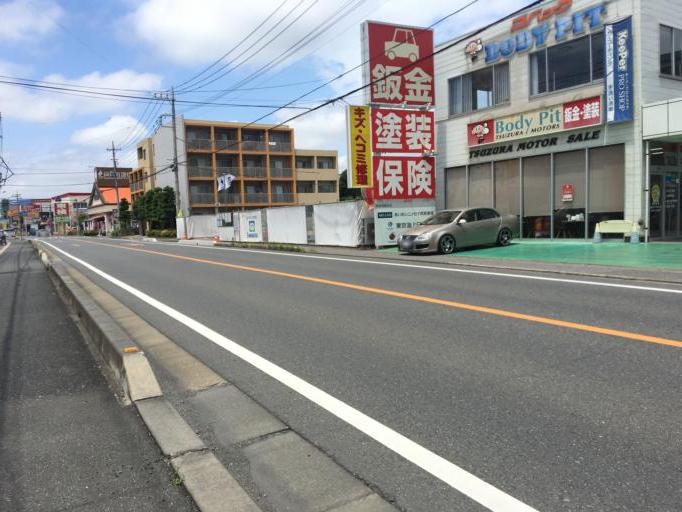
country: JP
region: Saitama
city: Okegawa
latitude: 35.9845
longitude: 139.5803
